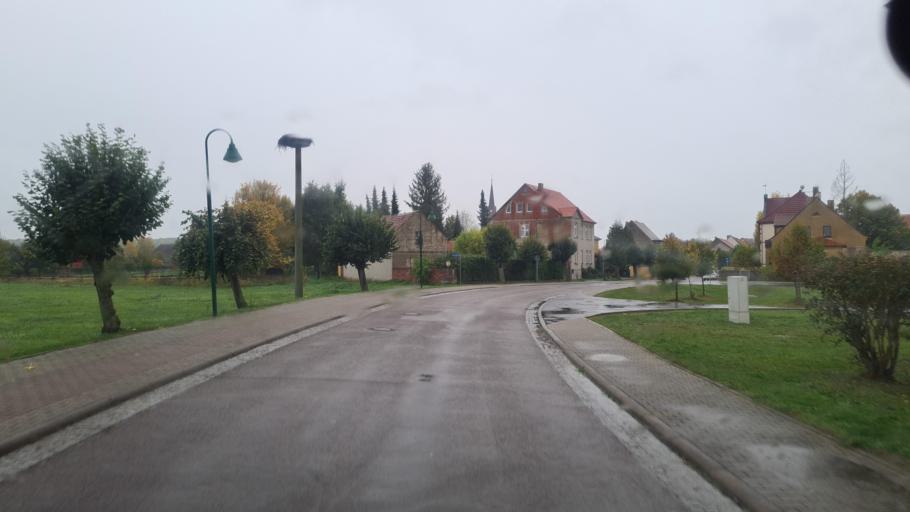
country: DE
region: Brandenburg
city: Schlieben
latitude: 51.7272
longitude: 13.3824
